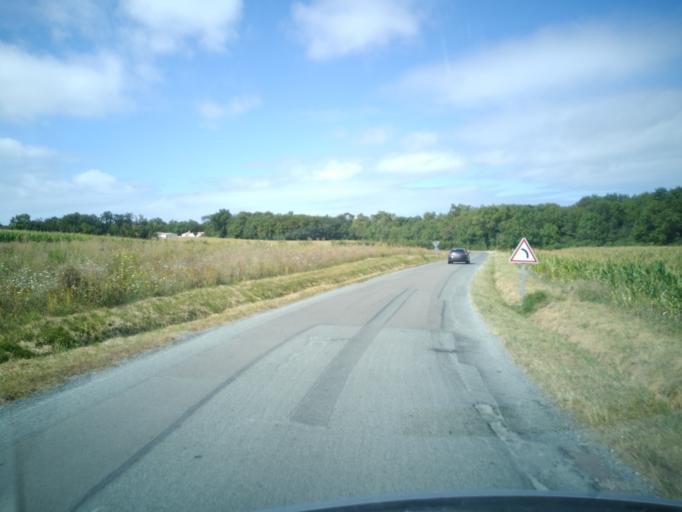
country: FR
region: Poitou-Charentes
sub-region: Departement de la Charente-Maritime
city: Breuillet
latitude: 45.7002
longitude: -1.0570
